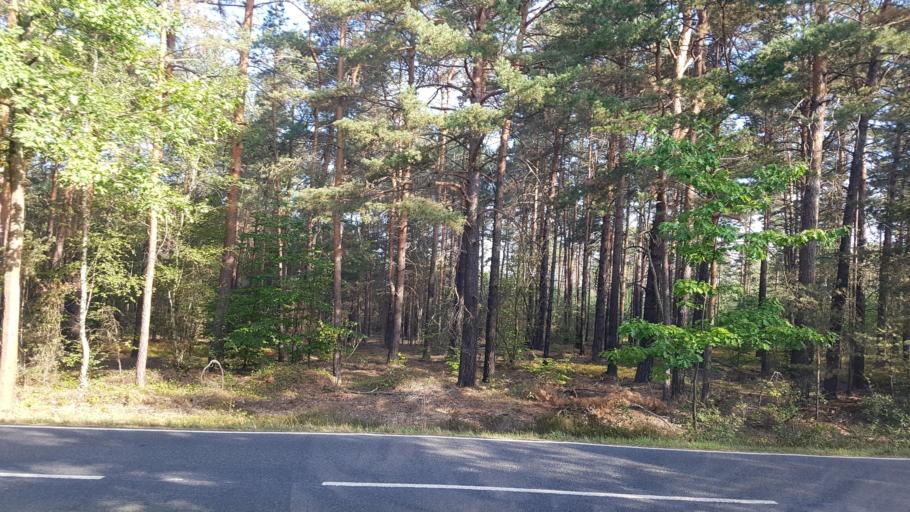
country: DE
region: Brandenburg
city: Sallgast
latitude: 51.5772
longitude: 13.8252
